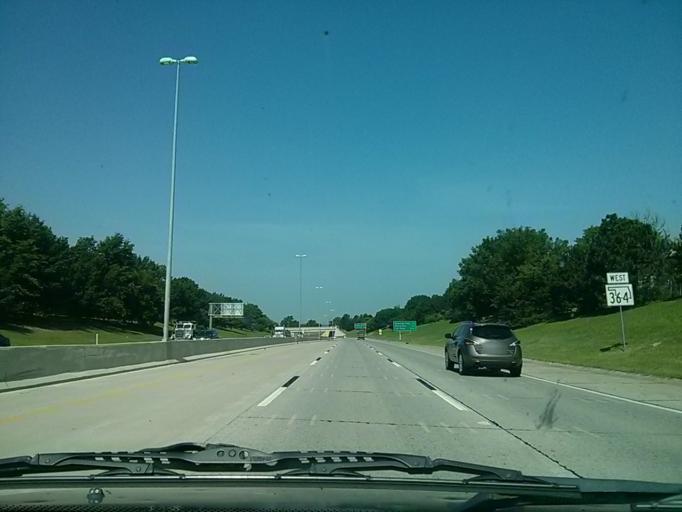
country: US
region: Oklahoma
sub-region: Tulsa County
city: Jenks
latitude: 36.0255
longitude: -95.9343
